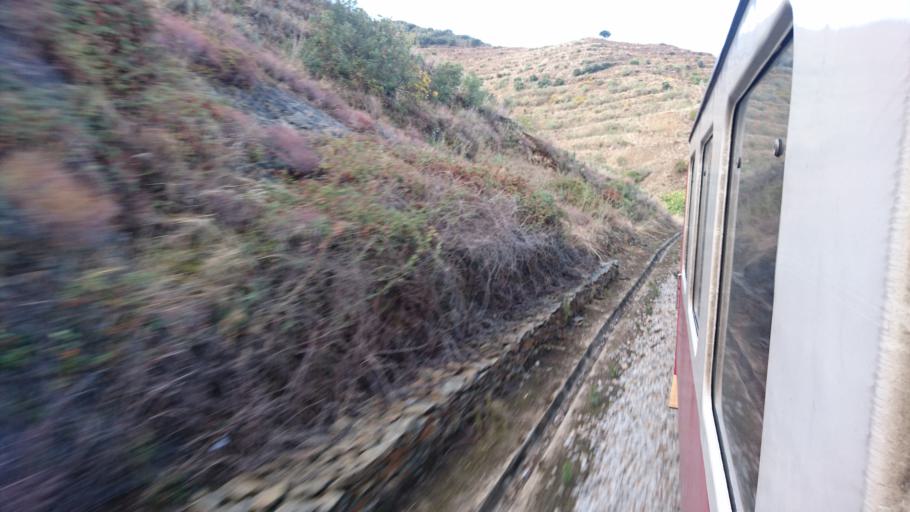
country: PT
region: Guarda
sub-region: Vila Nova de Foz Coa
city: Vila Nova de Foz Coa
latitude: 41.1234
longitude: -7.1641
